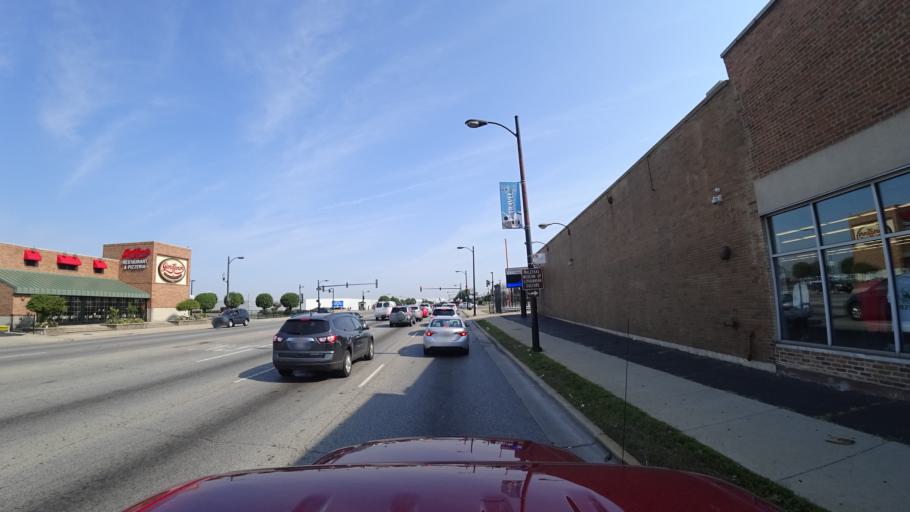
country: US
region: Illinois
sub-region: Cook County
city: Hometown
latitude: 41.7775
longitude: -87.7421
